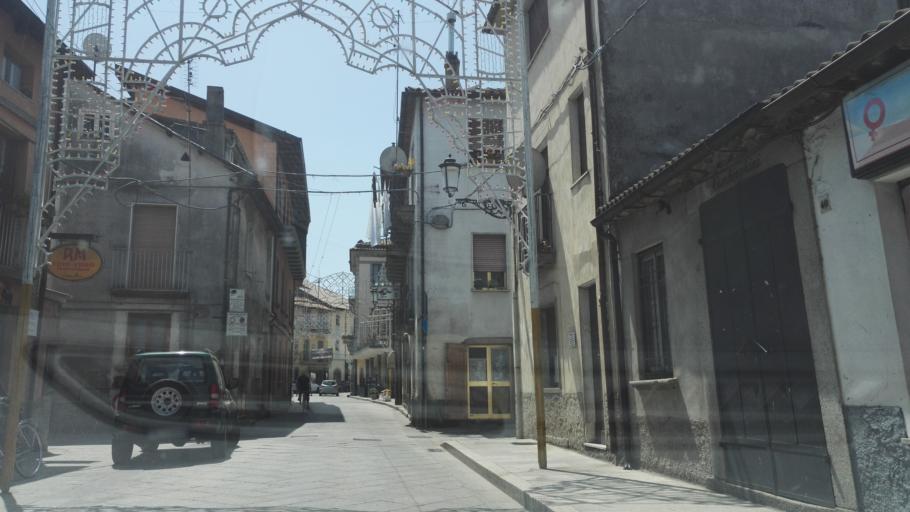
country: IT
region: Calabria
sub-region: Provincia di Vibo-Valentia
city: Serra San Bruno
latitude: 38.5799
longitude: 16.3320
